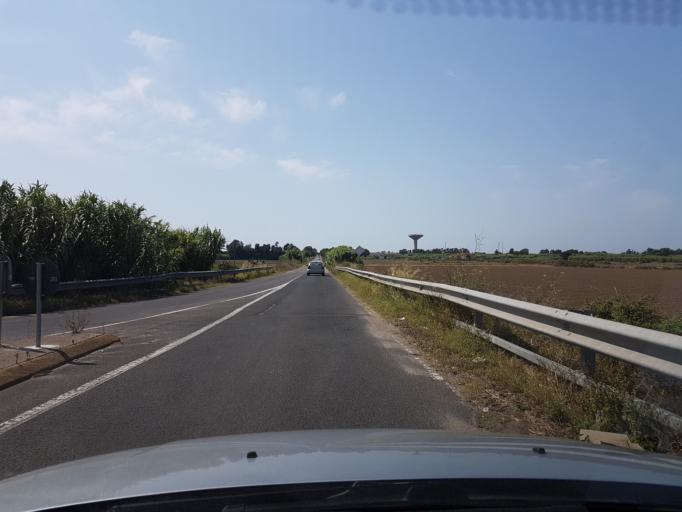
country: IT
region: Sardinia
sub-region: Provincia di Oristano
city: Solanas
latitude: 39.9180
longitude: 8.5537
